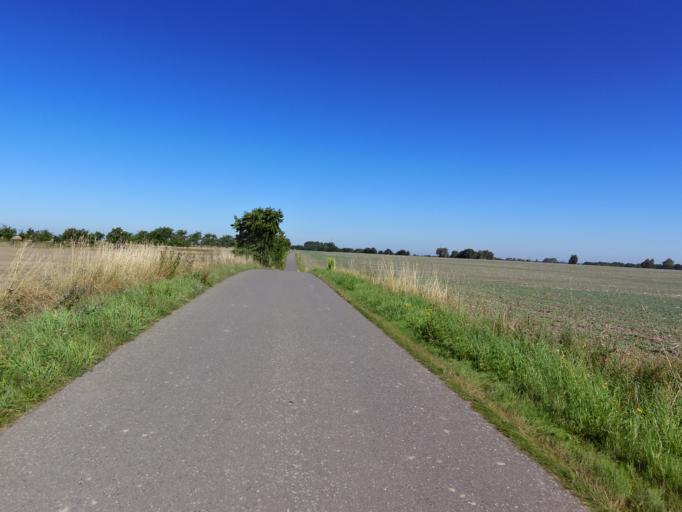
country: DE
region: Saxony
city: Dommitzsch
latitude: 51.6448
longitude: 12.8579
